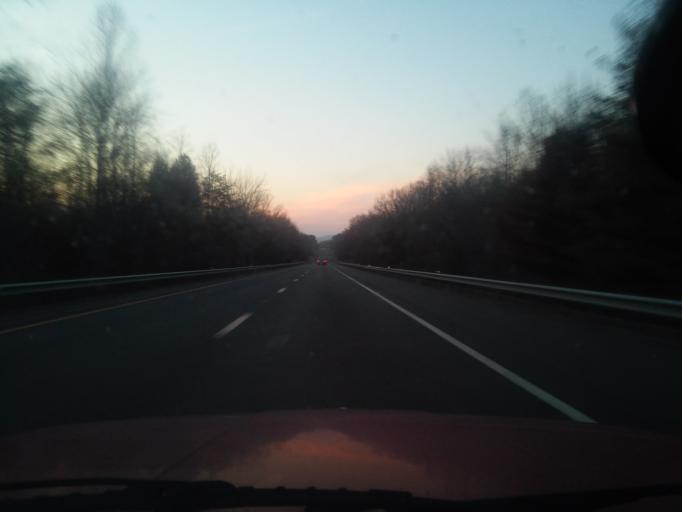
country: US
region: Virginia
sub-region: Fluvanna County
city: Lake Monticello
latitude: 37.9861
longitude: -78.2338
